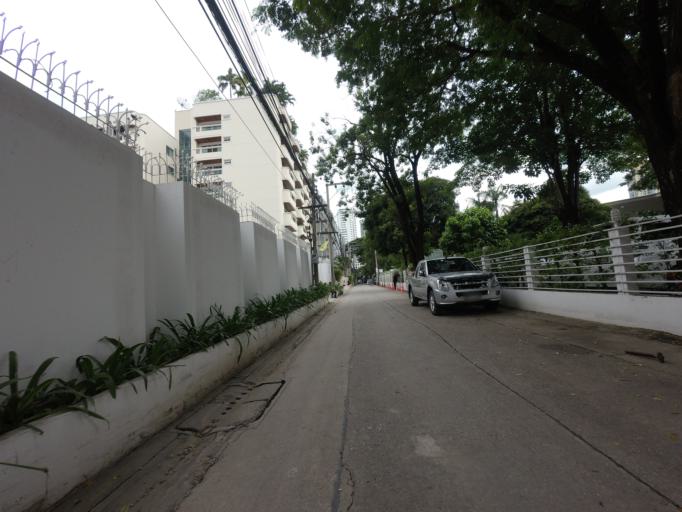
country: TH
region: Bangkok
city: Watthana
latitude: 13.7441
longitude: 100.5712
